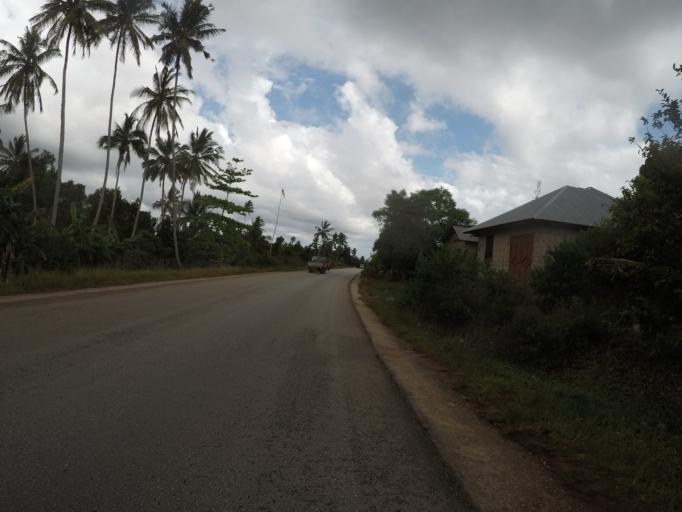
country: TZ
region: Zanzibar North
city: Gamba
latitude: -5.9464
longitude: 39.2543
